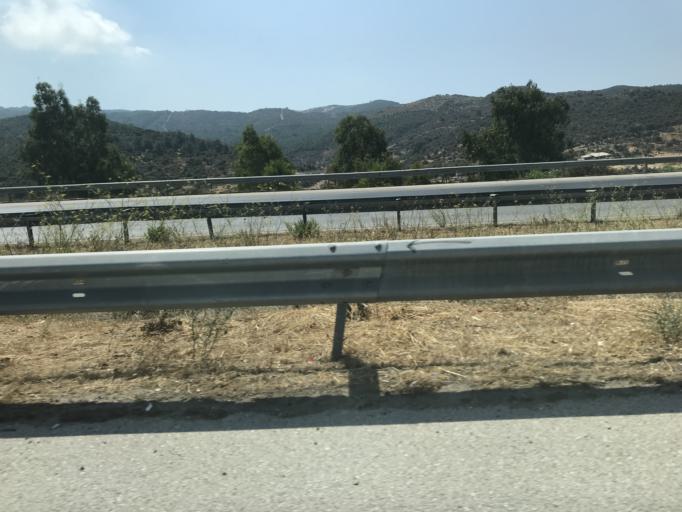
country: TR
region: Izmir
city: Urla
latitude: 38.3708
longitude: 26.9084
